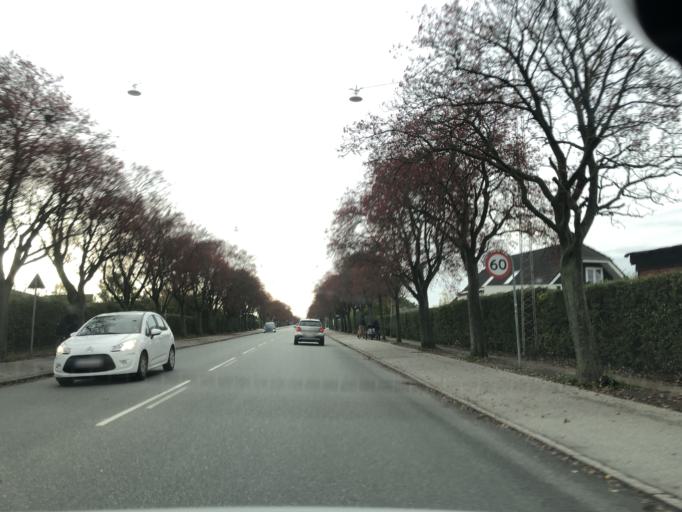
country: DK
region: Capital Region
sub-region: Tarnby Kommune
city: Tarnby
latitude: 55.6028
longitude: 12.5833
